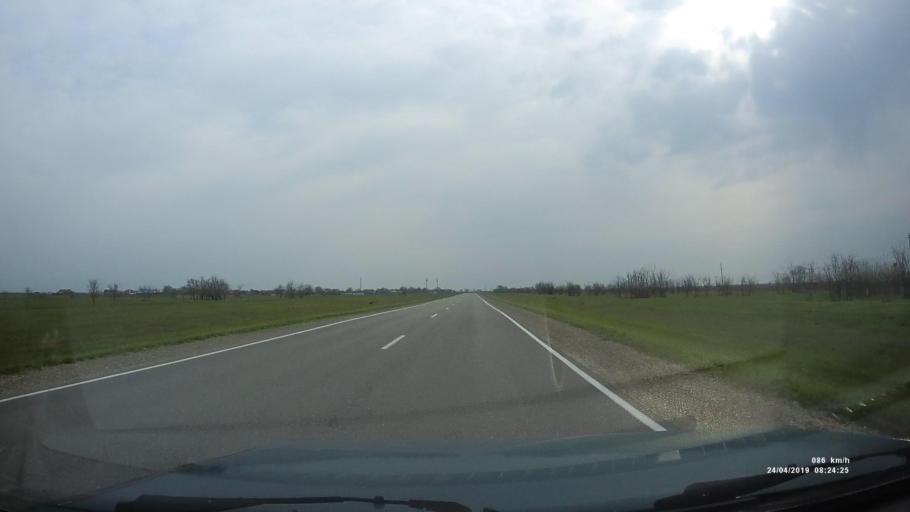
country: RU
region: Kalmykiya
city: Priyutnoye
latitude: 46.1205
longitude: 43.7543
